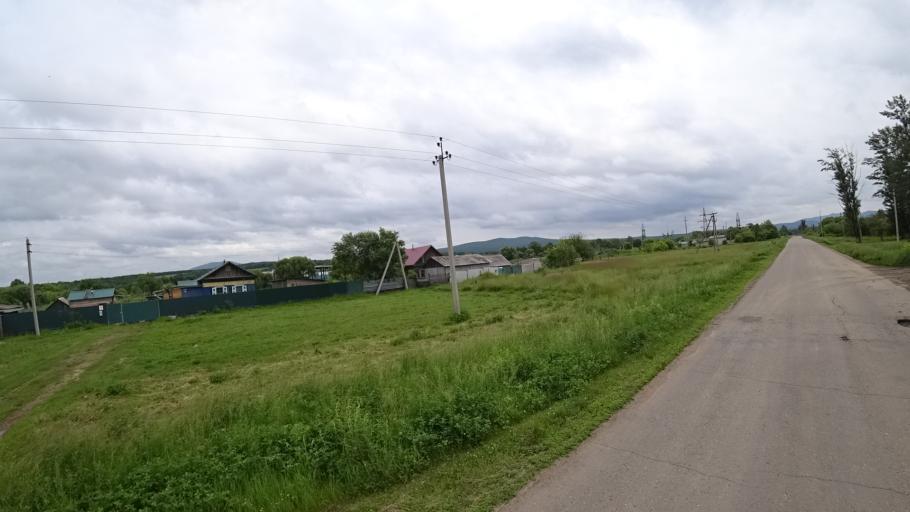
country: RU
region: Primorskiy
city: Novosysoyevka
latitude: 44.2360
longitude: 133.3699
